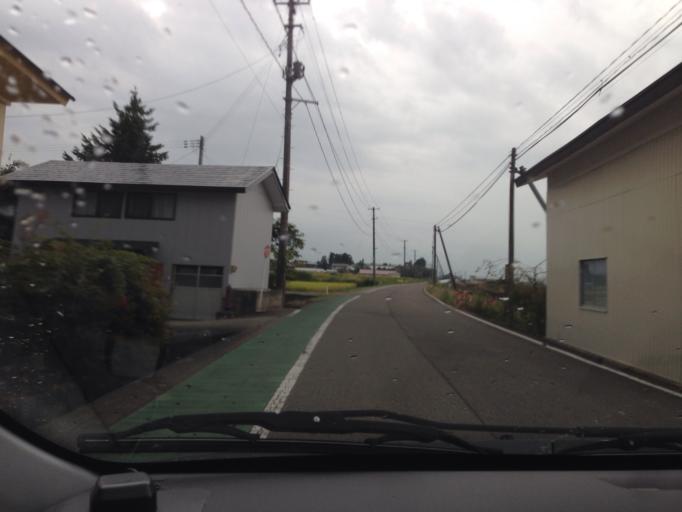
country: JP
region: Fukushima
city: Kitakata
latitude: 37.6078
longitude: 139.9140
